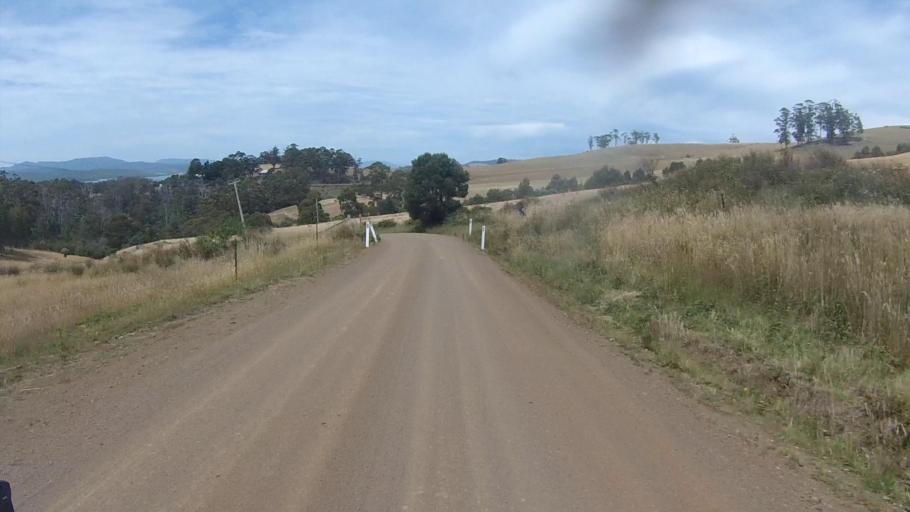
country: AU
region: Tasmania
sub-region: Sorell
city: Sorell
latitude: -42.7842
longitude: 147.8428
